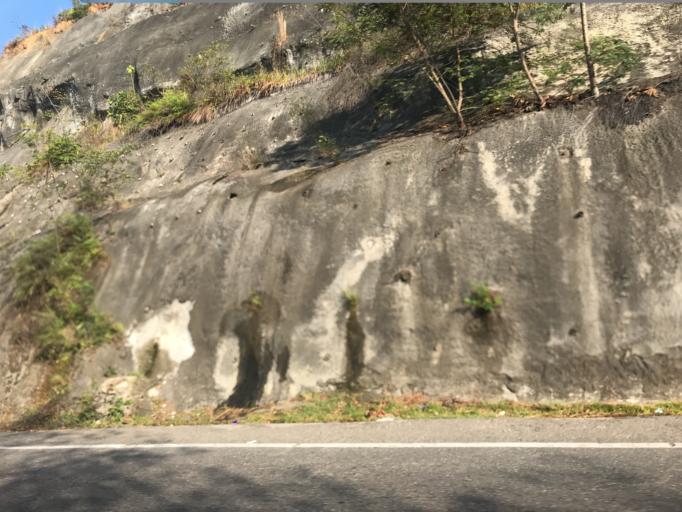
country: CO
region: Cundinamarca
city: Ricaurte
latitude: 4.2363
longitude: -74.7156
